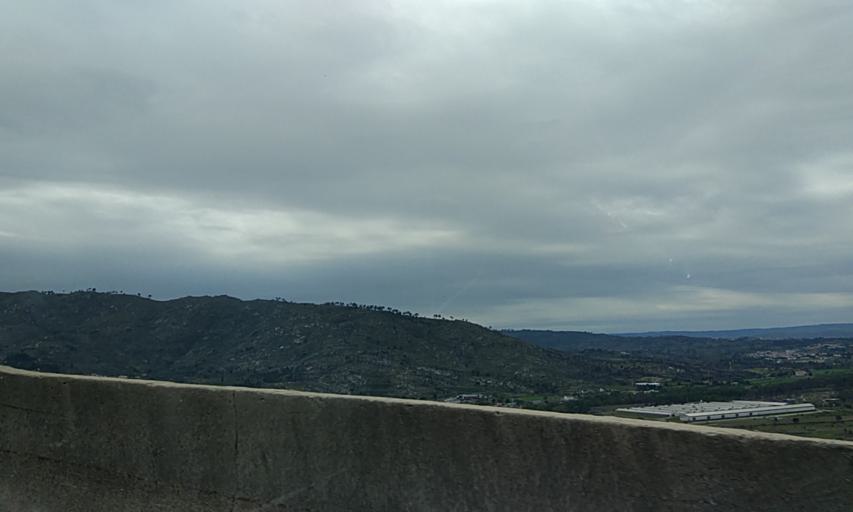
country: PT
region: Guarda
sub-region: Guarda
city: Guarda
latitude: 40.6136
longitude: -7.2834
